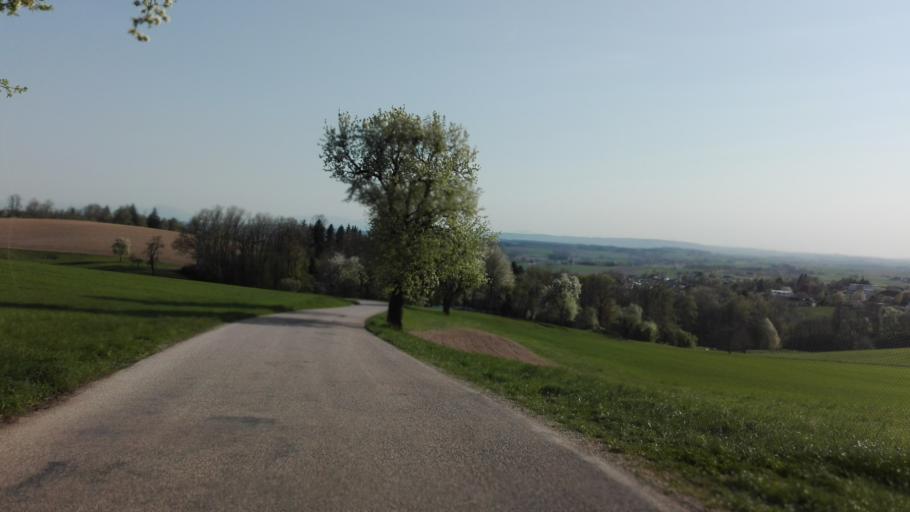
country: AT
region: Upper Austria
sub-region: Politischer Bezirk Grieskirchen
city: Grieskirchen
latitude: 48.3539
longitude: 13.7780
